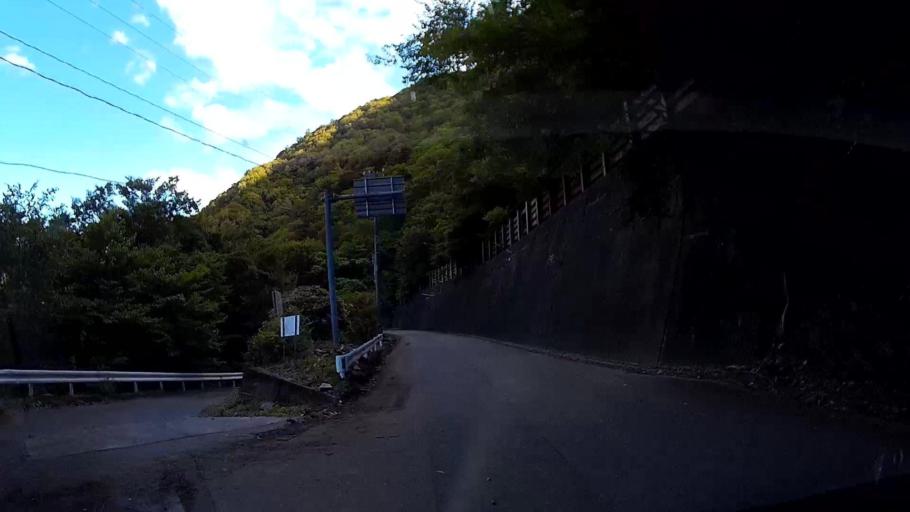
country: JP
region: Shizuoka
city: Shizuoka-shi
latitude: 35.2983
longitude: 138.2151
